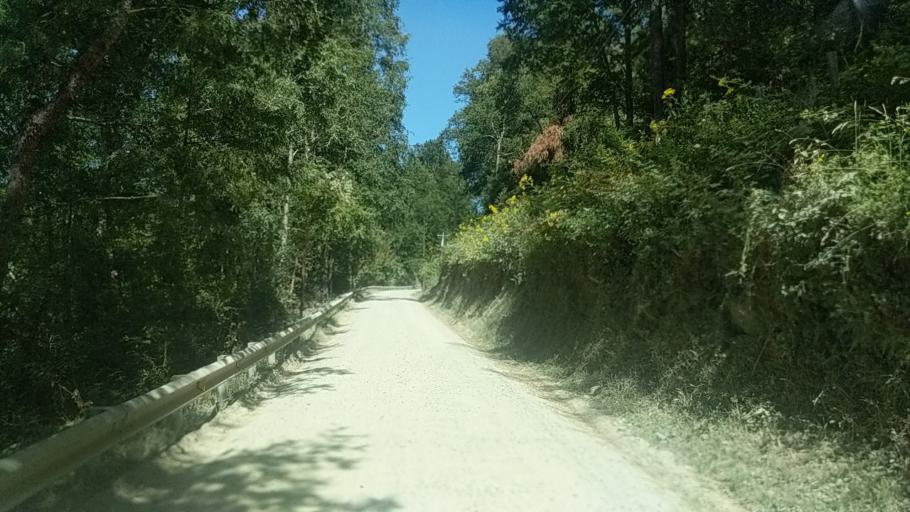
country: CL
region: Araucania
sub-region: Provincia de Cautin
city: Pucon
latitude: -39.0632
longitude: -71.7183
